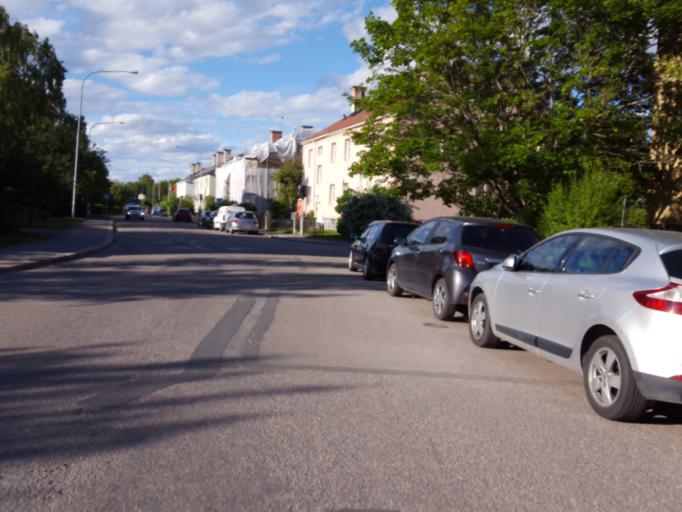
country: SE
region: Uppsala
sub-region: Uppsala Kommun
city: Uppsala
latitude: 59.8592
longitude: 17.6571
